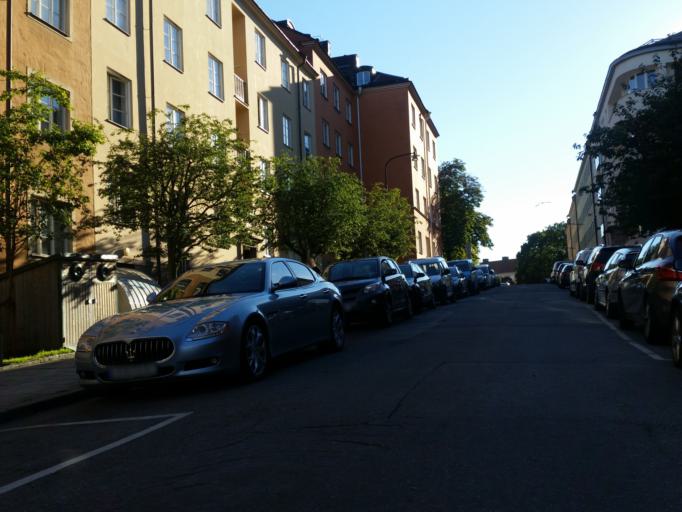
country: SE
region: Stockholm
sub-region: Stockholms Kommun
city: Stockholm
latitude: 59.3097
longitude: 18.0744
